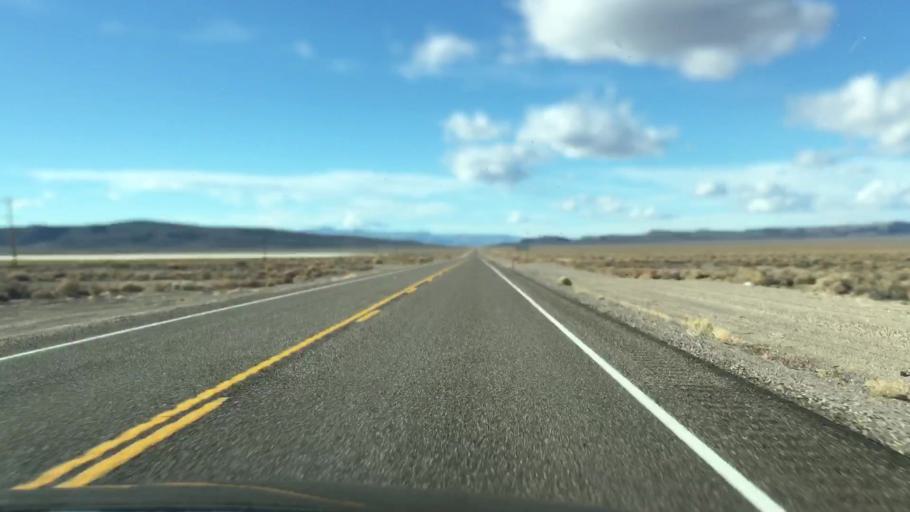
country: US
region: Nevada
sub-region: Nye County
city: Beatty
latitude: 37.1388
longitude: -116.8564
